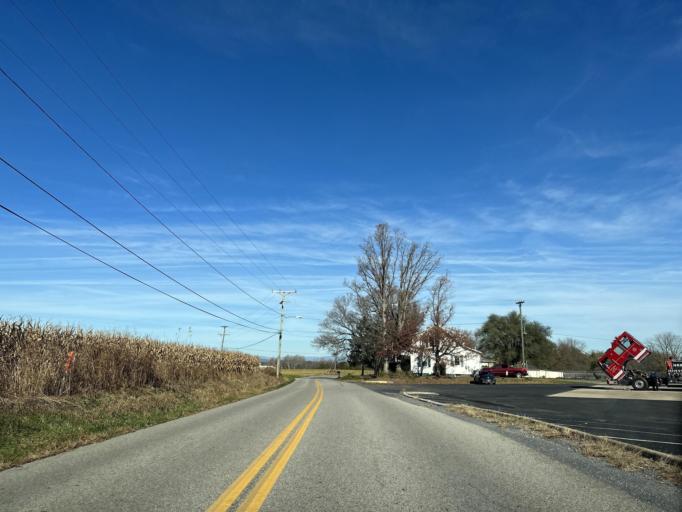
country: US
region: Virginia
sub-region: Augusta County
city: Crimora
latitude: 38.2010
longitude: -78.9043
